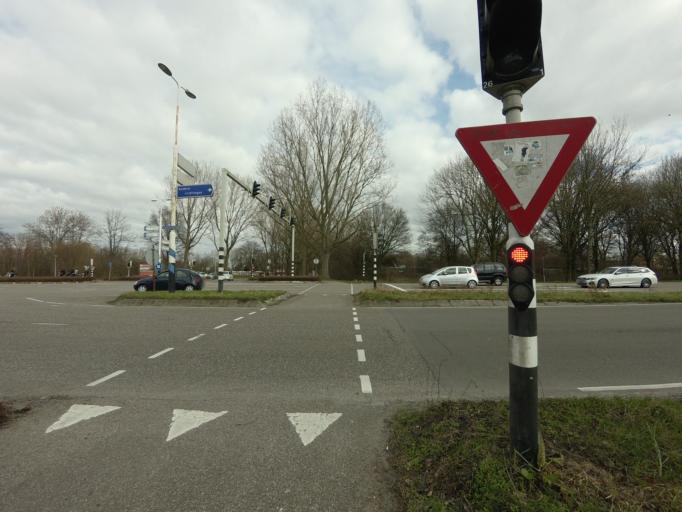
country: NL
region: South Holland
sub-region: Gemeente Alphen aan den Rijn
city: Alphen aan den Rijn
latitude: 52.1295
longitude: 4.6723
